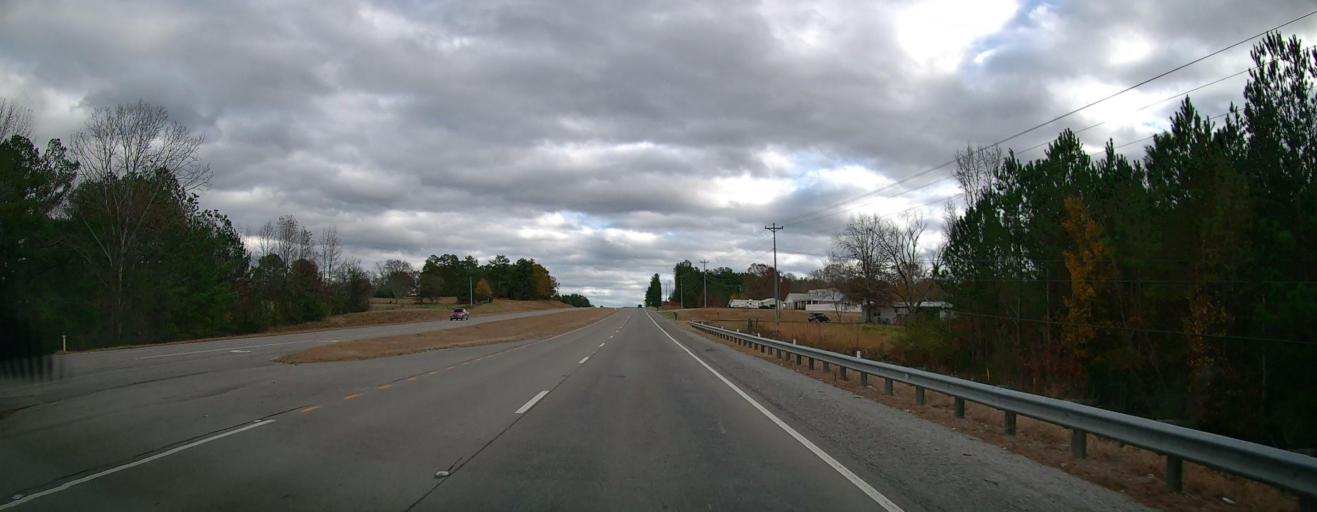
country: US
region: Alabama
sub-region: Lawrence County
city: Town Creek
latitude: 34.5814
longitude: -87.4117
